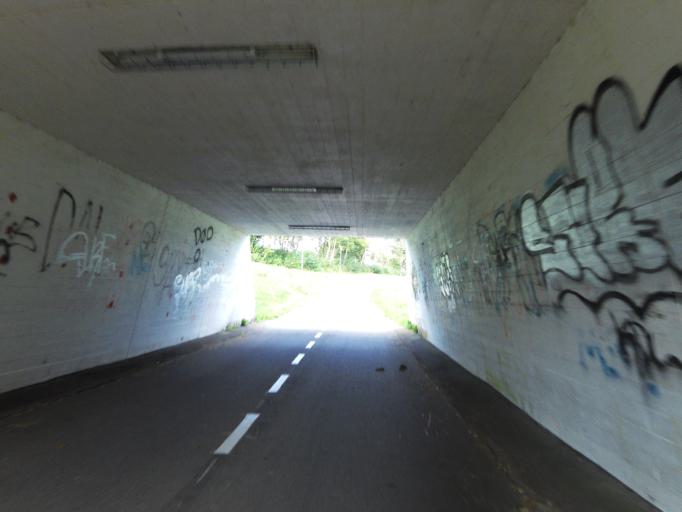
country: DK
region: South Denmark
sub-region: Vejen Kommune
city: Vejen
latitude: 55.4633
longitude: 9.1280
